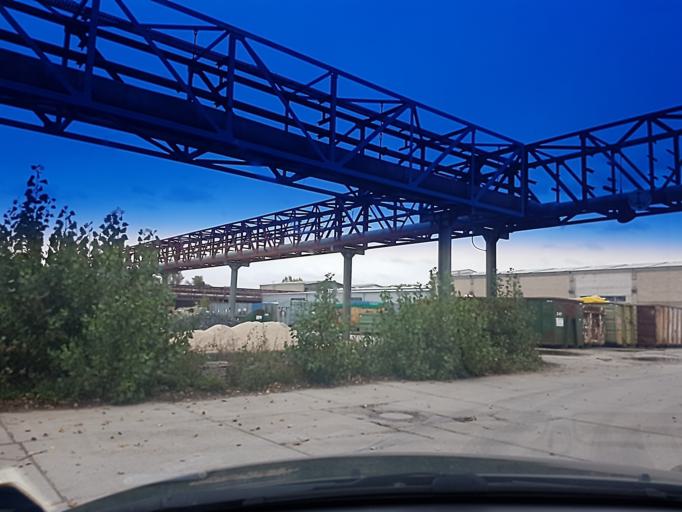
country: DE
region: Bavaria
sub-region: Upper Franconia
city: Zapfendorf
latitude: 50.0192
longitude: 10.9281
